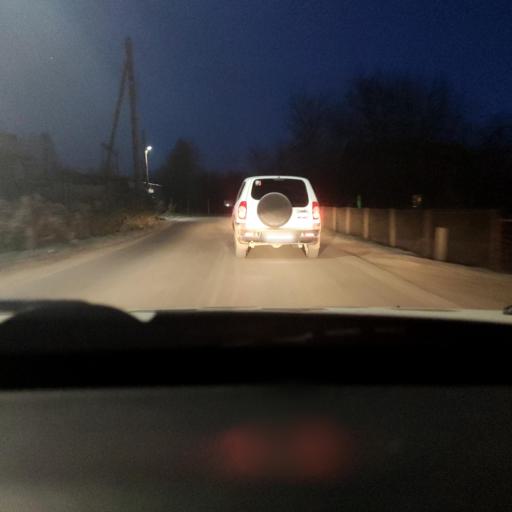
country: RU
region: Perm
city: Ferma
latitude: 57.8998
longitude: 56.3007
